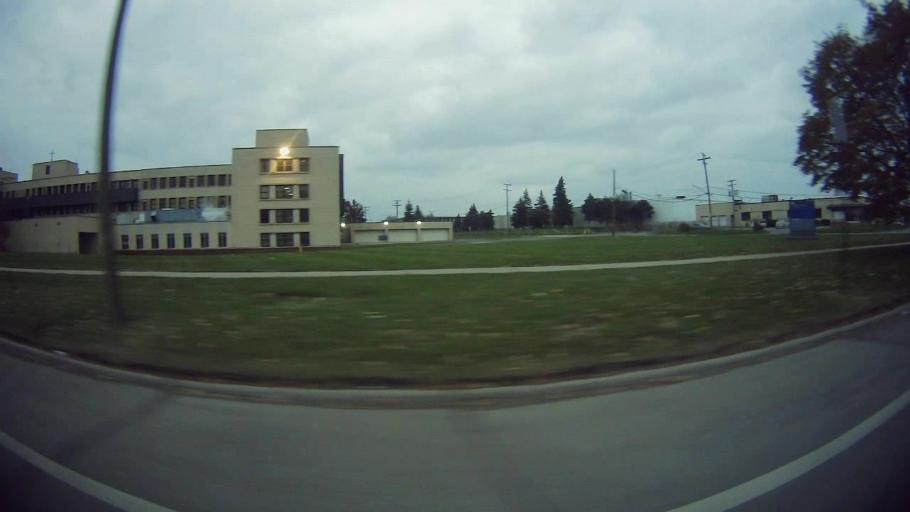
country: US
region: Michigan
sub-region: Macomb County
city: Warren
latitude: 42.4413
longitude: -83.0190
